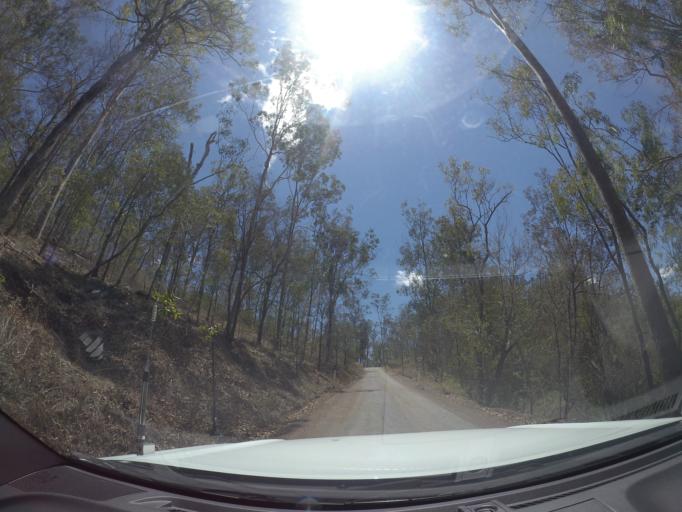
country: AU
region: Queensland
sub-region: Ipswich
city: Springfield Lakes
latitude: -27.8057
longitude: 152.8438
